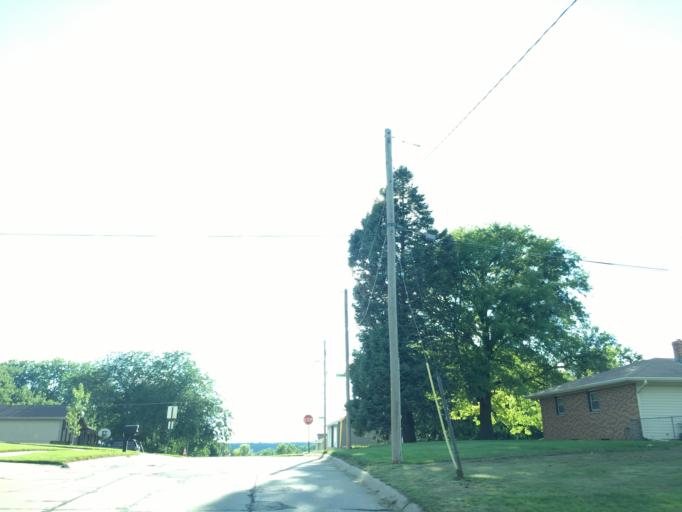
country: US
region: Nebraska
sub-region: Sarpy County
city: La Vista
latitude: 41.1877
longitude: -95.9858
